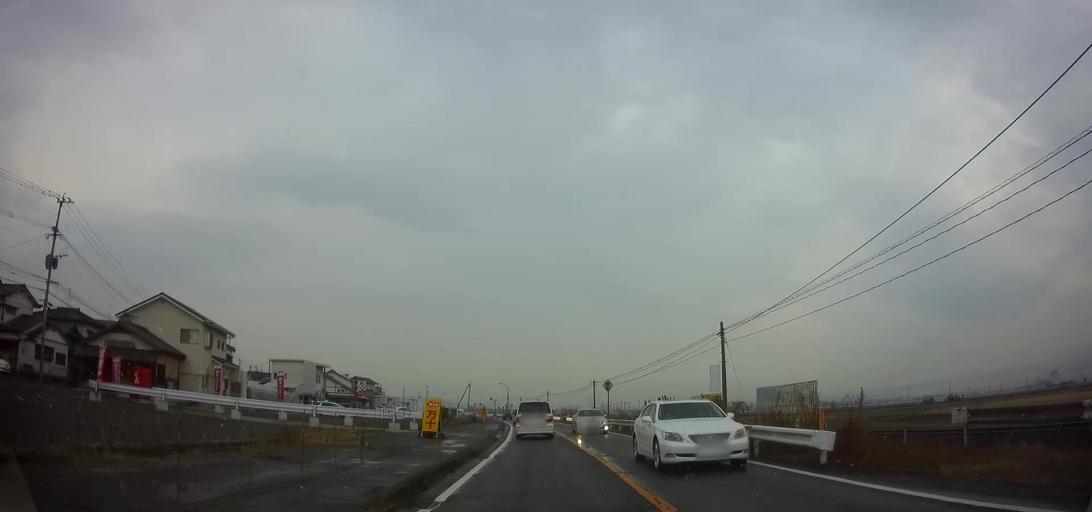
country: JP
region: Nagasaki
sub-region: Isahaya-shi
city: Isahaya
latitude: 32.8377
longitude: 130.1034
